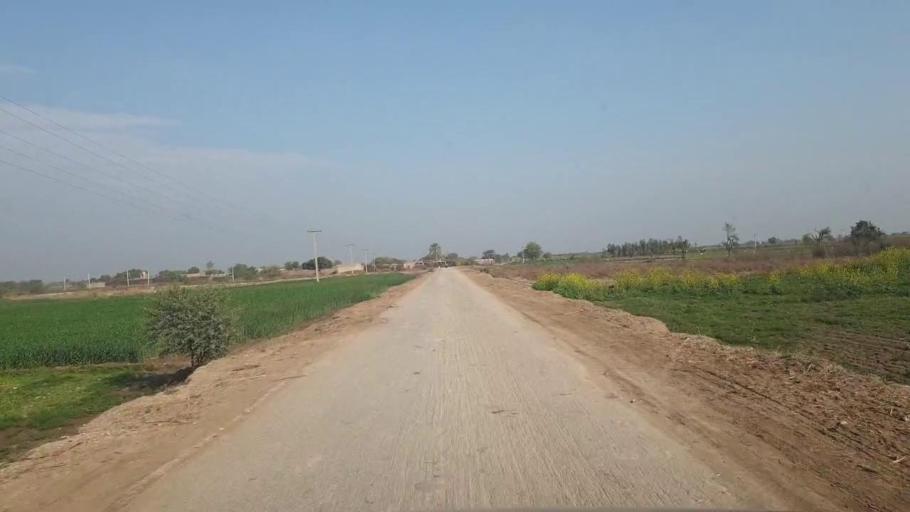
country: PK
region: Sindh
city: Tando Adam
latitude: 25.7435
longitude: 68.6070
